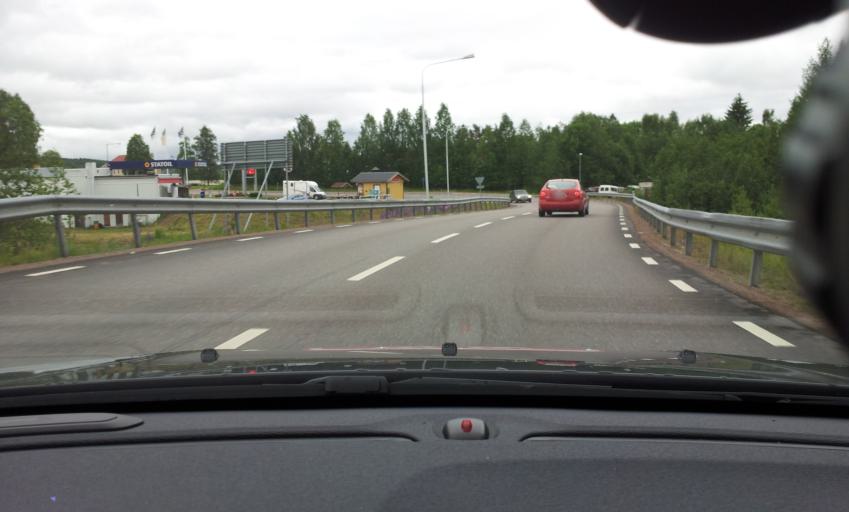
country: SE
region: Jaemtland
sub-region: Ragunda Kommun
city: Hammarstrand
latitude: 63.0112
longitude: 16.6617
